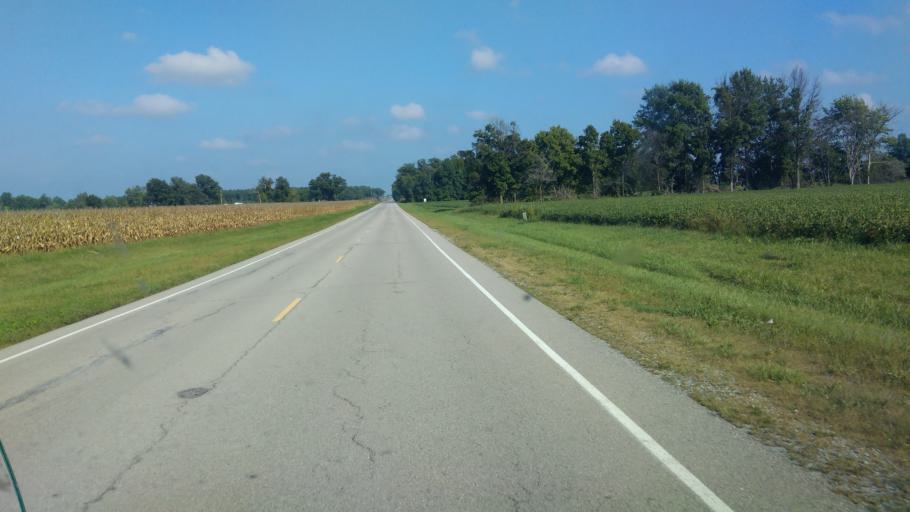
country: US
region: Ohio
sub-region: Hancock County
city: Arlington
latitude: 40.8339
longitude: -83.6396
